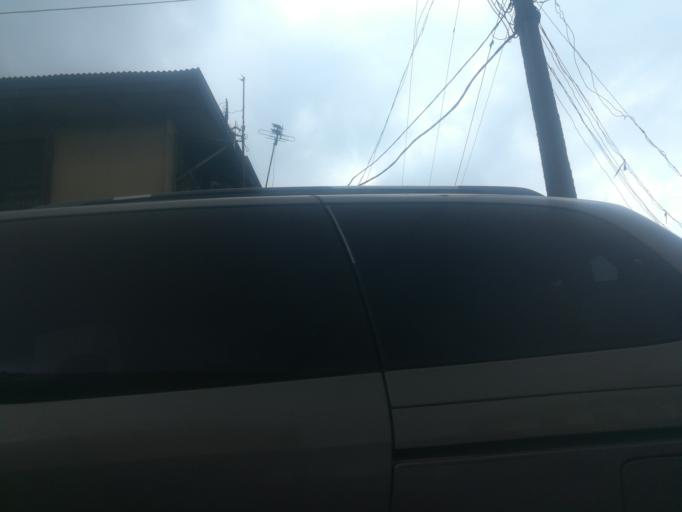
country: NG
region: Lagos
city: Ojota
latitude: 6.5938
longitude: 3.3854
